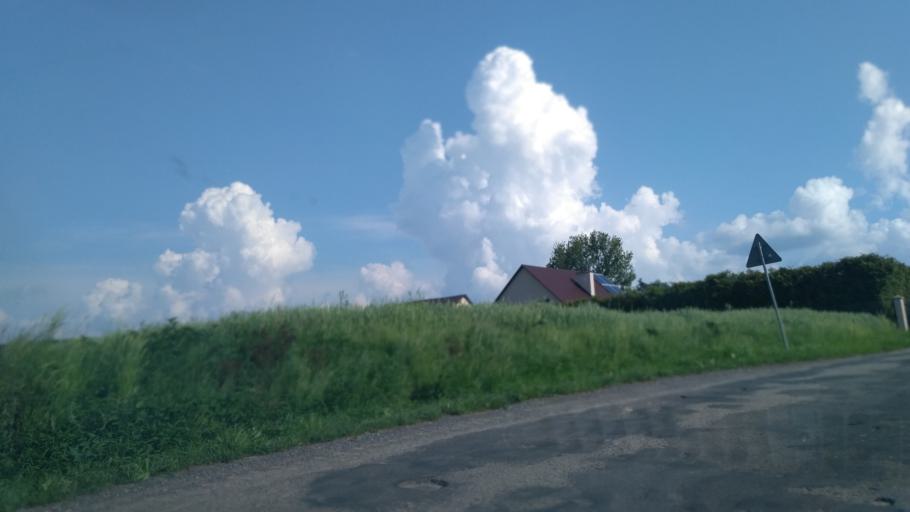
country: PL
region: Subcarpathian Voivodeship
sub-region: Powiat jaroslawski
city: Kramarzowka
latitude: 49.8688
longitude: 22.5128
